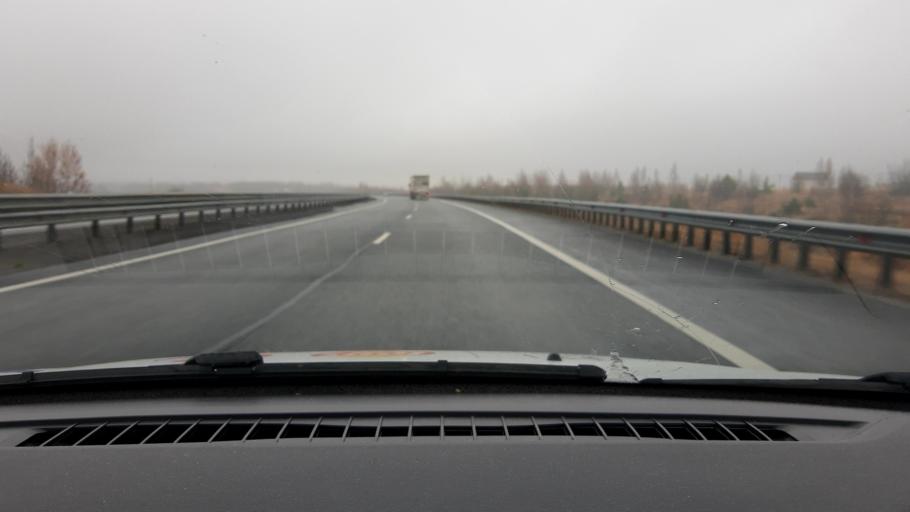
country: RU
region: Nizjnij Novgorod
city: Burevestnik
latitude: 56.1506
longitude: 43.7493
